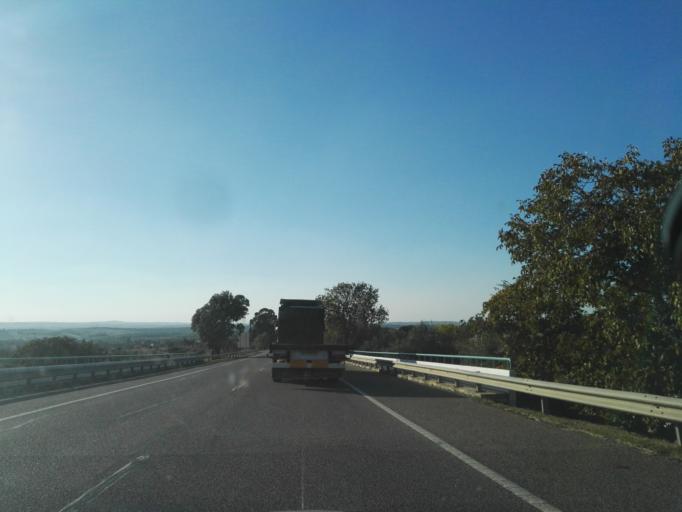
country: PT
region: Portalegre
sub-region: Elvas
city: Elvas
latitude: 38.8603
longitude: -7.2918
